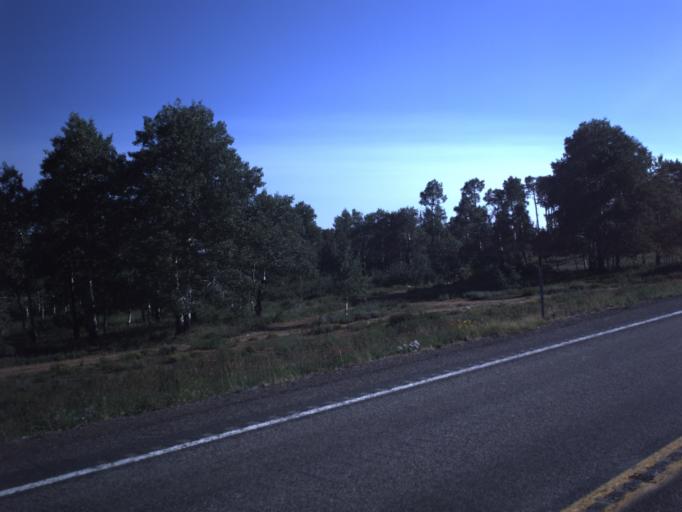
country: US
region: Utah
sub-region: Sanpete County
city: Fairview
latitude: 39.6710
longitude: -111.3236
